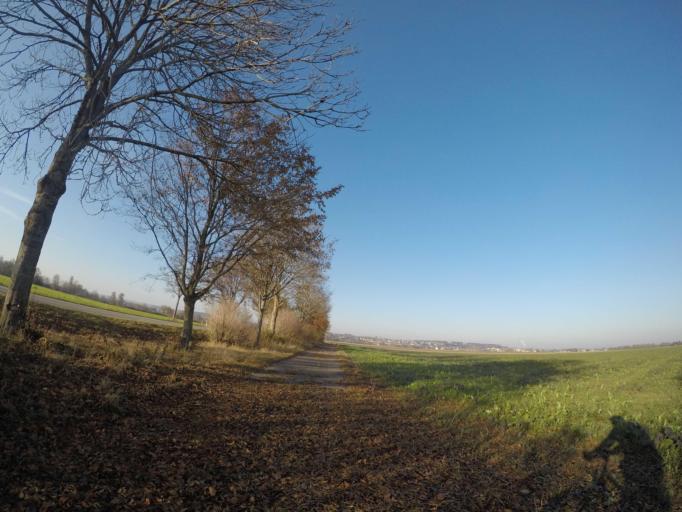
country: DE
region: Baden-Wuerttemberg
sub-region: Tuebingen Region
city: Unterstadion
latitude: 48.2160
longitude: 9.6879
